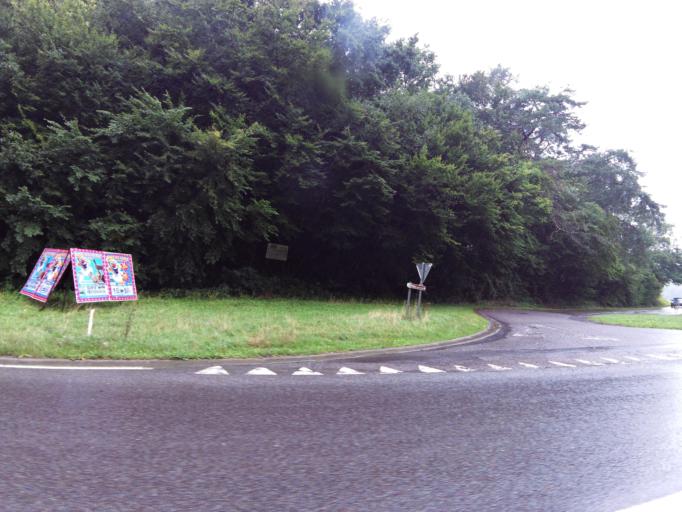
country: BE
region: Wallonia
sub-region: Province de Namur
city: Rochefort
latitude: 50.1622
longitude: 5.2453
